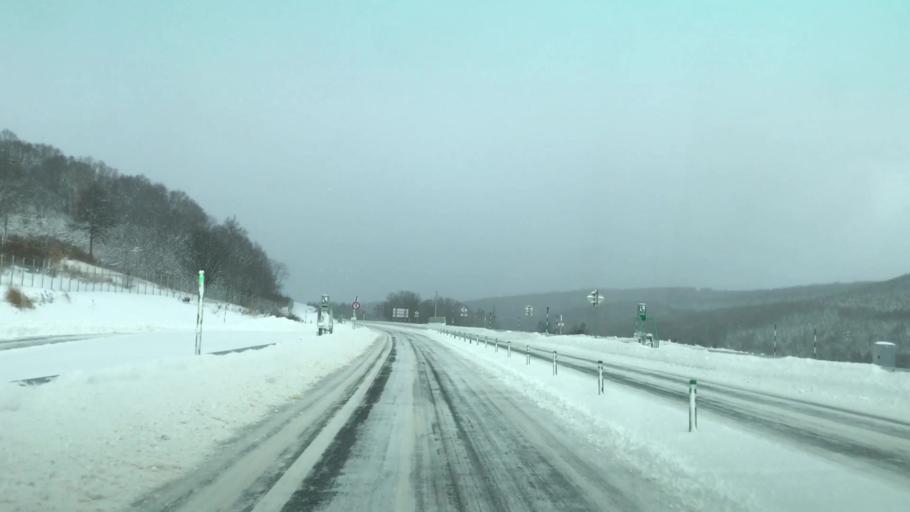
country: JP
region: Hokkaido
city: Otaru
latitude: 43.1965
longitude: 140.9510
